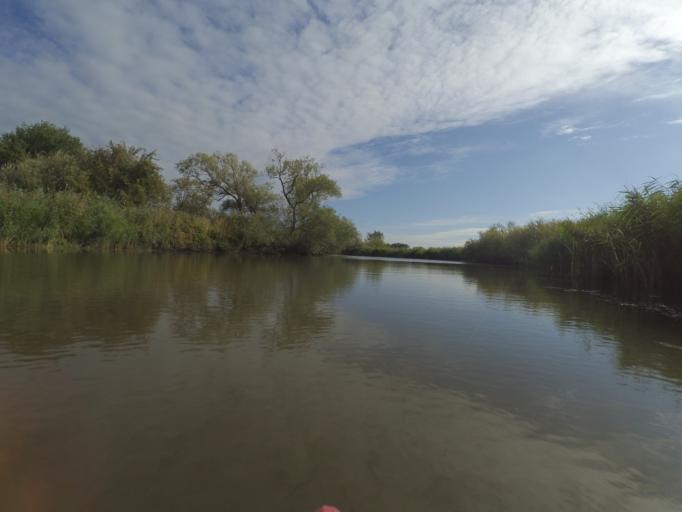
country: NL
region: North Brabant
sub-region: Gemeente Geertruidenberg
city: Geertruidenberg
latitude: 51.7236
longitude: 4.8415
